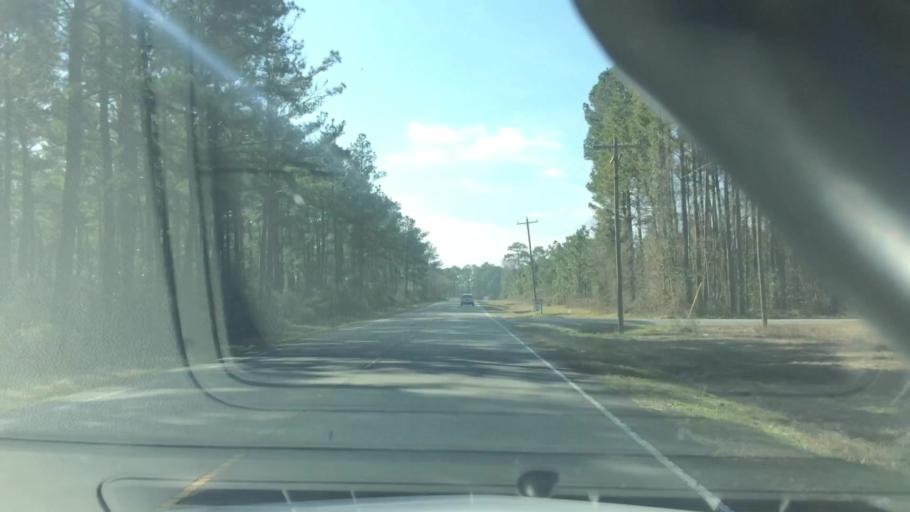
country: US
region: North Carolina
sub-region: Duplin County
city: Wallace
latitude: 34.7944
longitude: -77.8638
